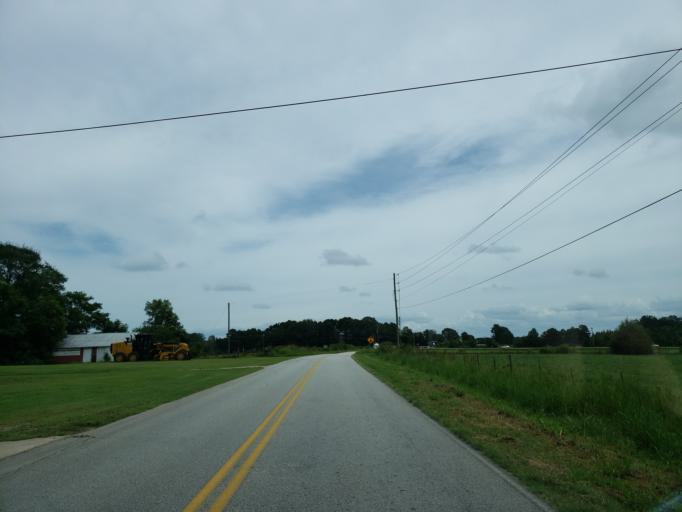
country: US
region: Georgia
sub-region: Butts County
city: Jackson
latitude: 33.2389
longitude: -84.0286
